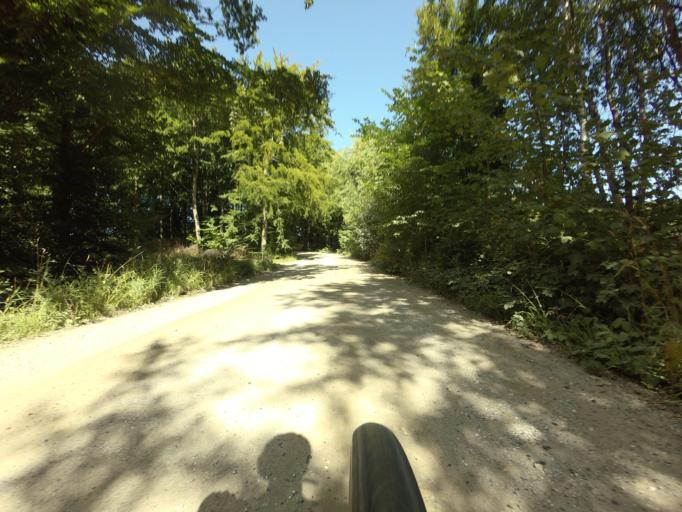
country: DK
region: Zealand
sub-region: Vordingborg Kommune
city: Stege
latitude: 54.9767
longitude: 12.5256
